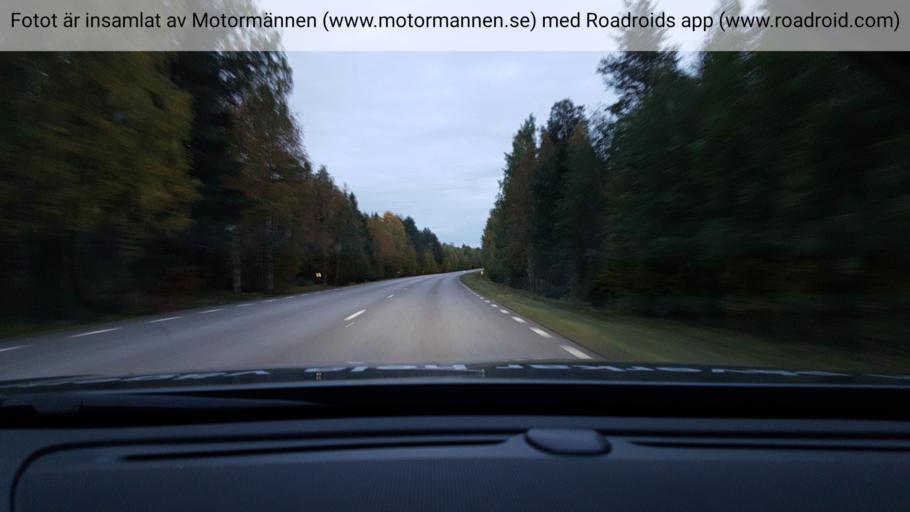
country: SE
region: Norrbotten
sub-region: Alvsbyns Kommun
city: AElvsbyn
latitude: 65.7996
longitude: 20.6412
